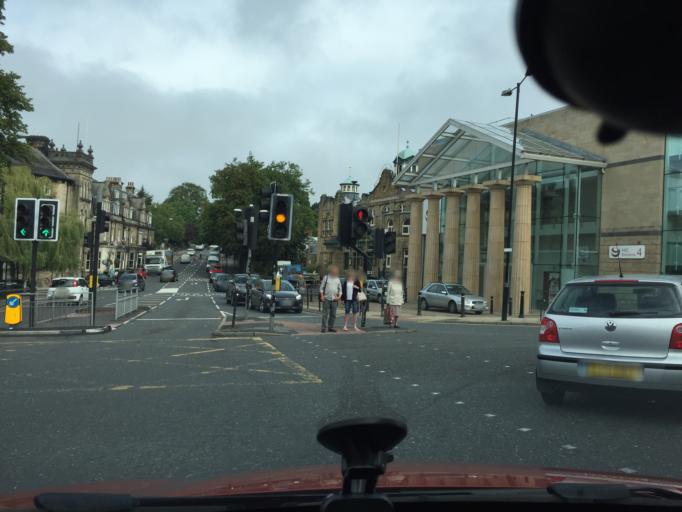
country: GB
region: England
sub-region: North Yorkshire
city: Harrogate
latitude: 53.9947
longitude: -1.5440
